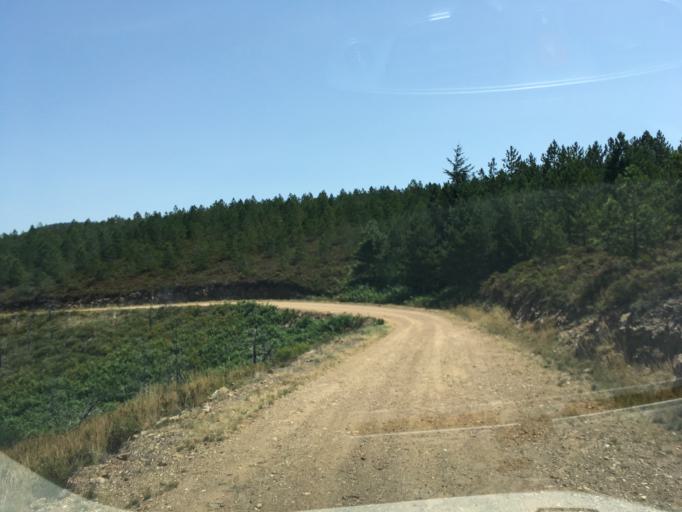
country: PT
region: Porto
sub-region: Baiao
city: Valadares
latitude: 41.2692
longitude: -7.9520
